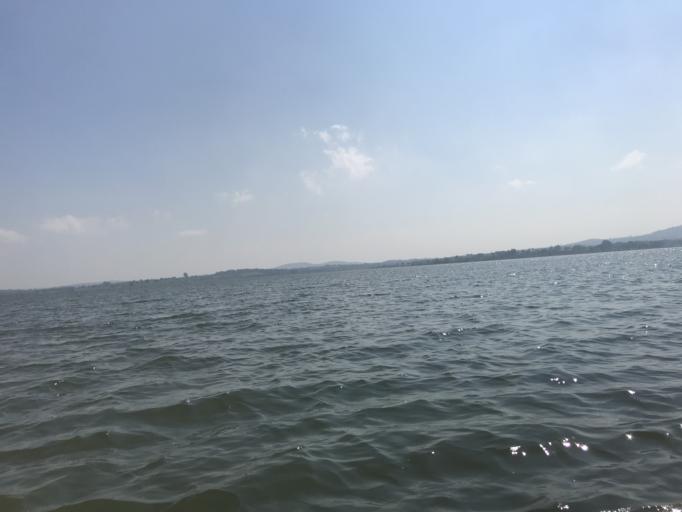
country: IN
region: Karnataka
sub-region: Mysore
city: Sargur
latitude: 11.9355
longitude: 76.2714
